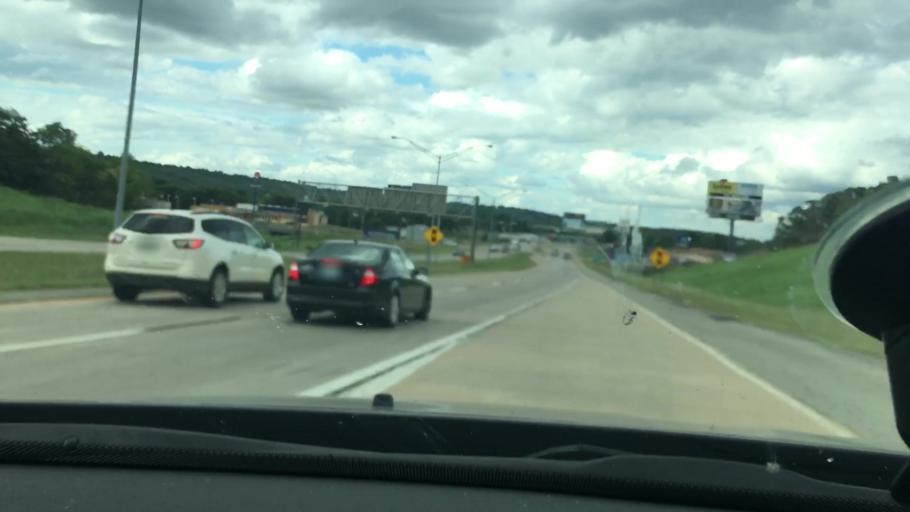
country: US
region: Oklahoma
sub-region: Okmulgee County
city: Henryetta
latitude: 35.4368
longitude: -95.9707
